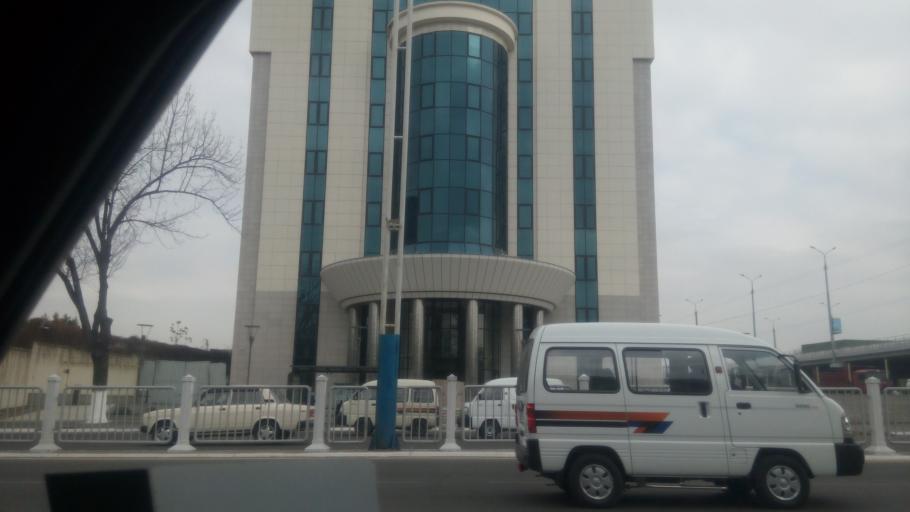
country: UZ
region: Toshkent Shahri
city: Tashkent
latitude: 41.3338
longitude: 69.2844
